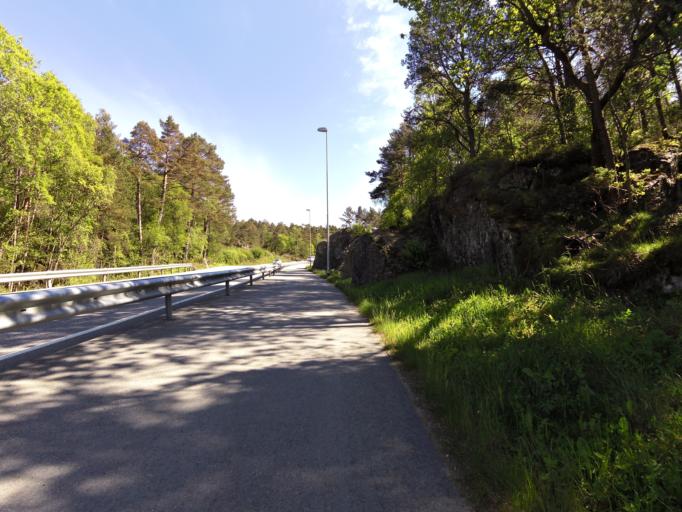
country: NO
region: Hordaland
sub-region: Stord
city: Sagvag
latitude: 59.7866
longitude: 5.3730
